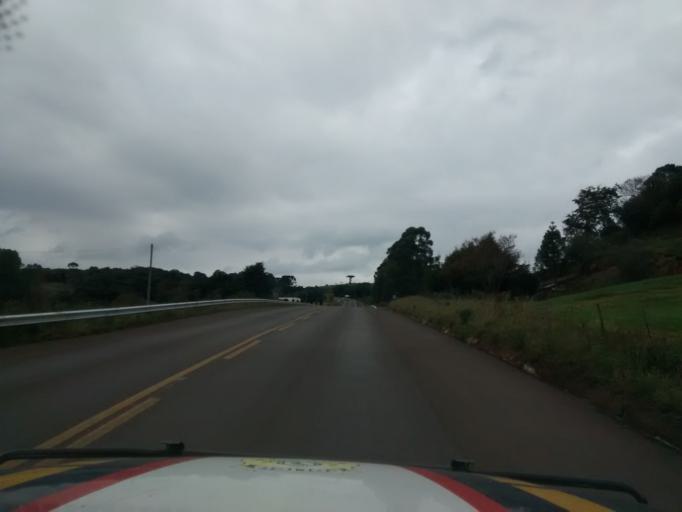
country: BR
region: Rio Grande do Sul
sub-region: Lagoa Vermelha
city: Lagoa Vermelha
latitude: -28.2283
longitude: -51.6226
